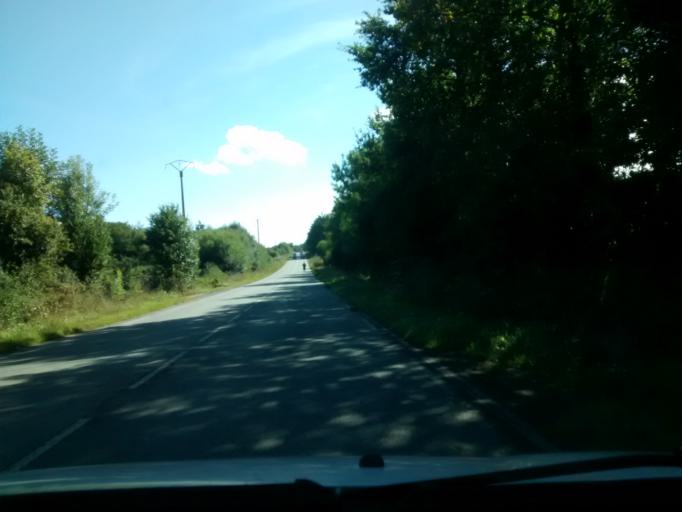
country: FR
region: Brittany
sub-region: Departement d'Ille-et-Vilaine
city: Saint-Lunaire
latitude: 48.6130
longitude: -2.0928
